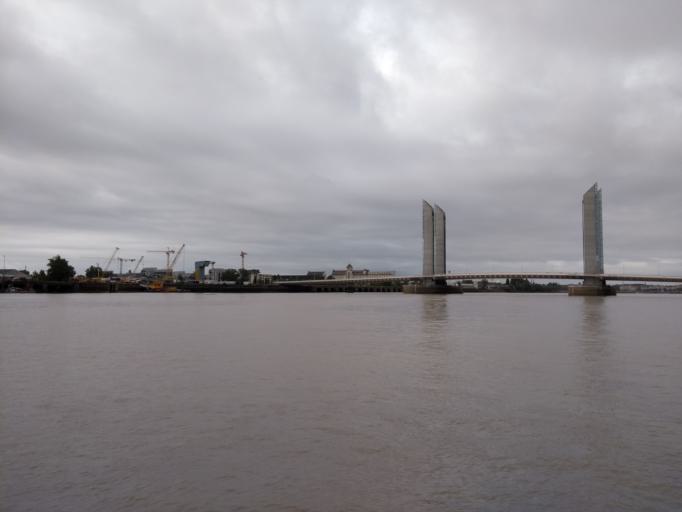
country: FR
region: Aquitaine
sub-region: Departement de la Gironde
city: Cenon
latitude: 44.8615
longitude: -0.5481
